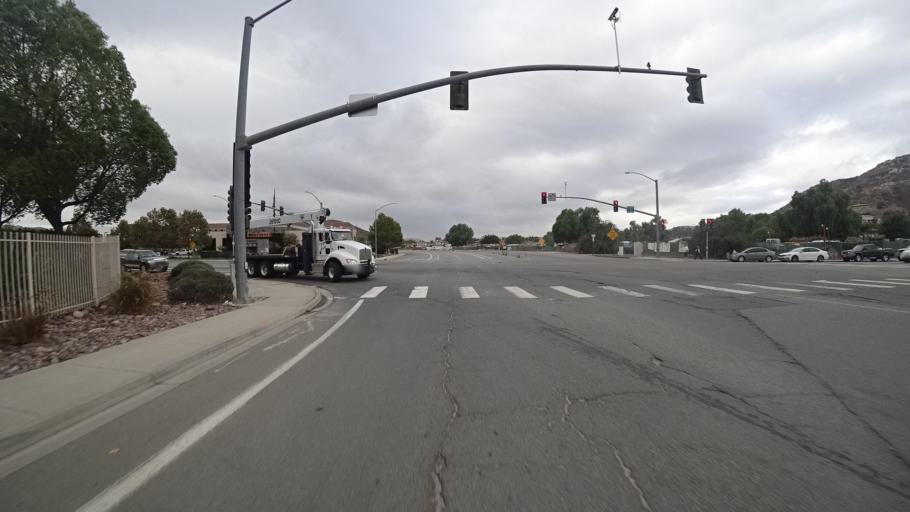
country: US
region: California
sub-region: San Diego County
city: Eucalyptus Hills
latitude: 32.8606
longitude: -116.9470
